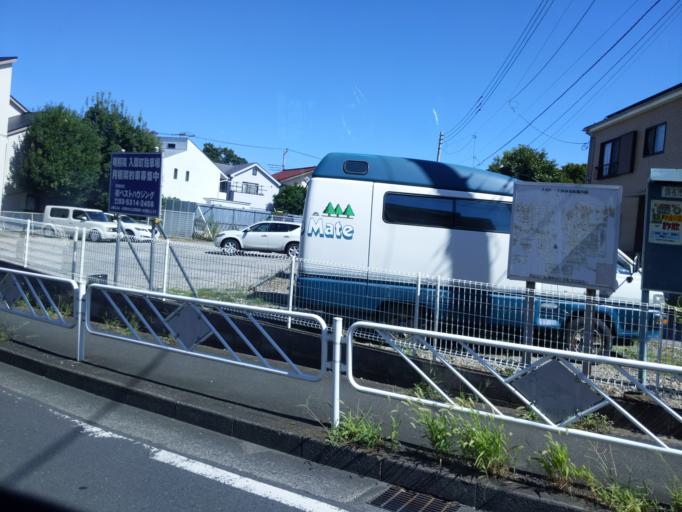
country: JP
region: Tokyo
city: Chofugaoka
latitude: 35.6498
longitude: 139.5907
